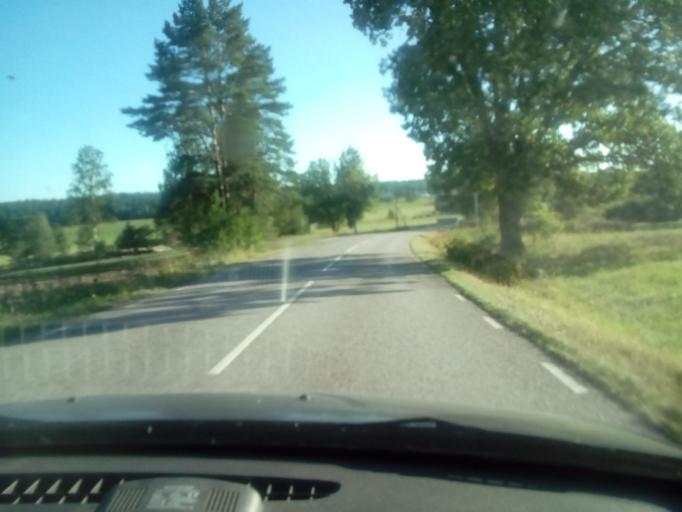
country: SE
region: Kalmar
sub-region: Vasterviks Kommun
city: Gamleby
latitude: 57.7892
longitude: 16.4097
